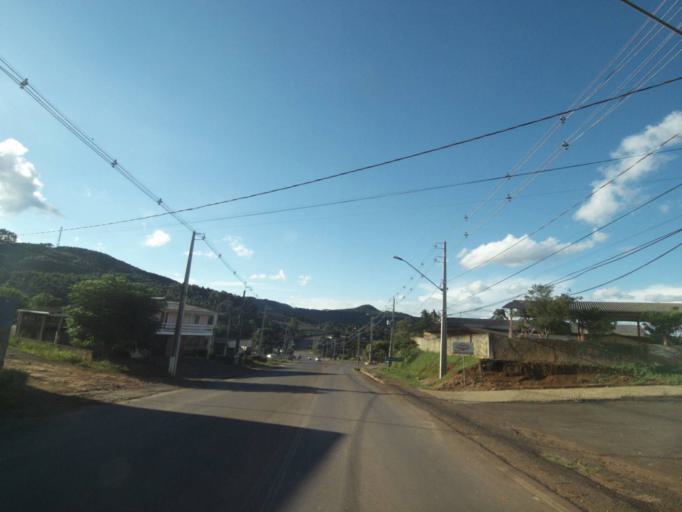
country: BR
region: Parana
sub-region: Uniao Da Vitoria
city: Uniao da Vitoria
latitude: -26.1618
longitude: -51.5376
